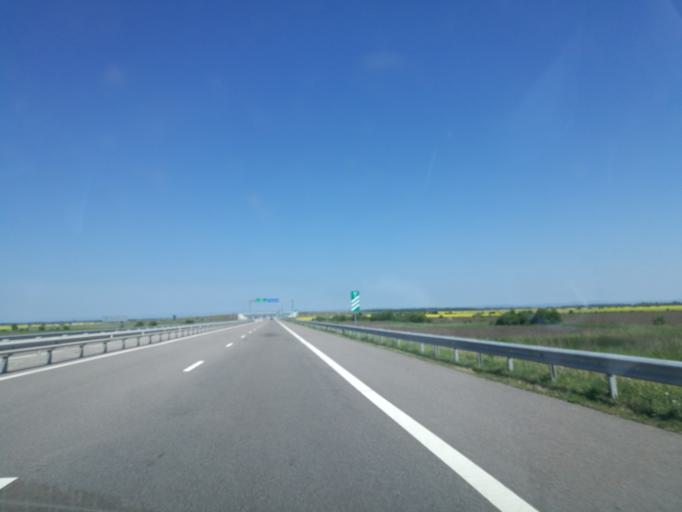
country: RO
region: Prahova
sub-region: Comuna Gherghita
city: Gherghita
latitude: 44.7697
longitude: 26.2509
